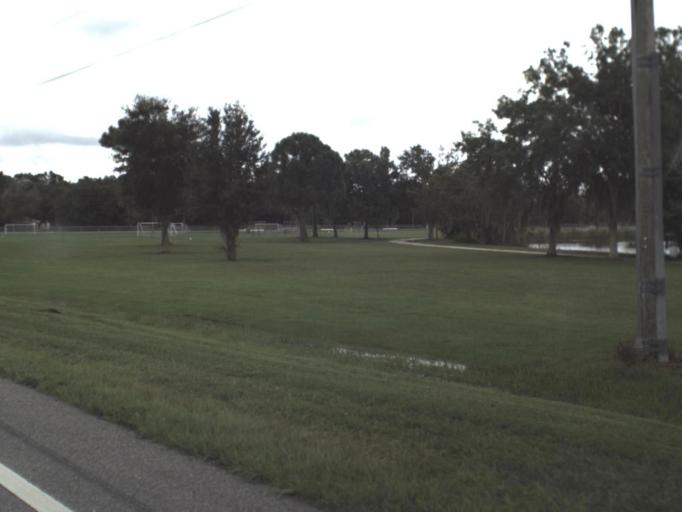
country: US
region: Florida
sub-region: Sarasota County
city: Lake Sarasota
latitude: 27.2690
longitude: -82.4364
